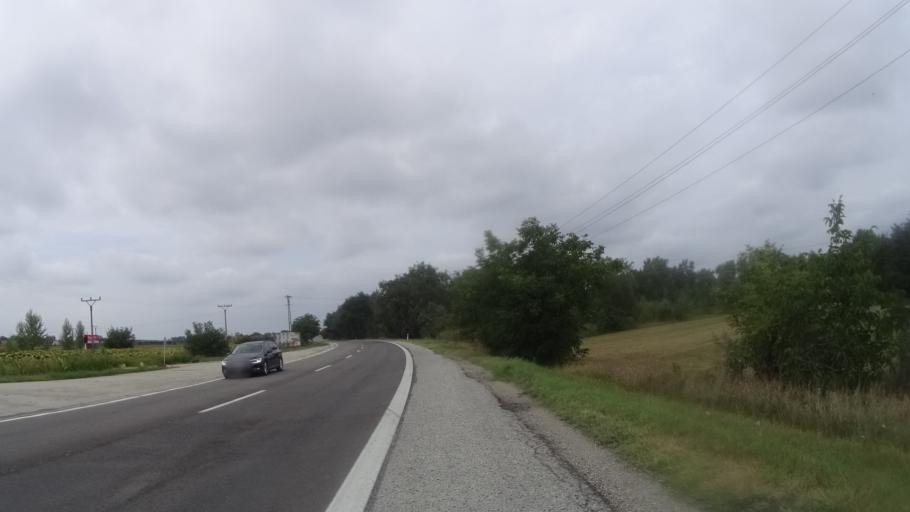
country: HU
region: Komarom-Esztergom
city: Acs
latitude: 47.7661
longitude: 18.0342
